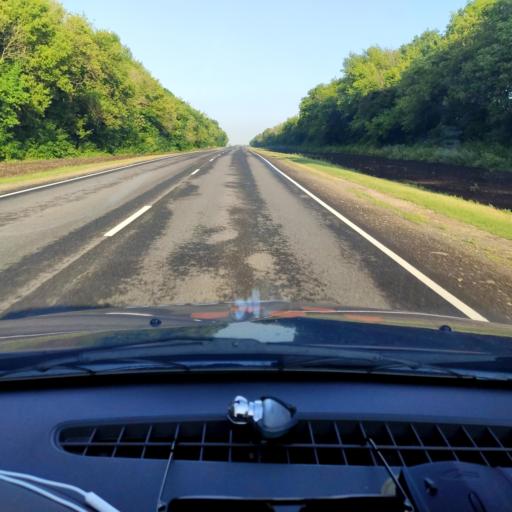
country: RU
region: Orjol
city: Livny
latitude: 52.4308
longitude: 37.8186
